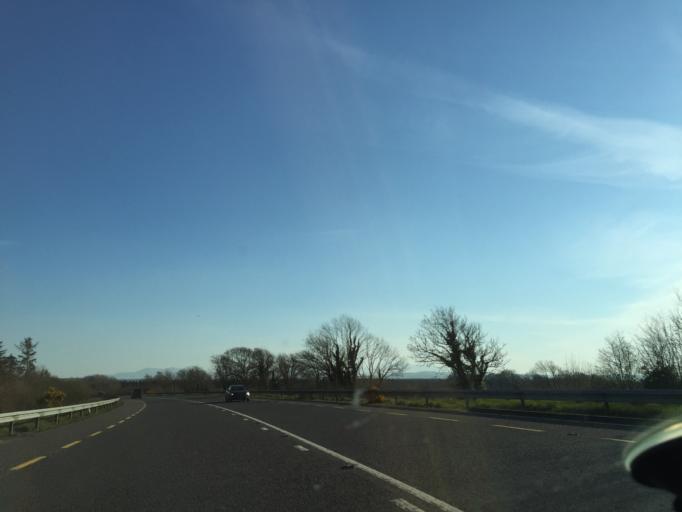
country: IE
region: Munster
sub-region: Ciarrai
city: Castleisland
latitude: 52.2006
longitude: -9.5711
